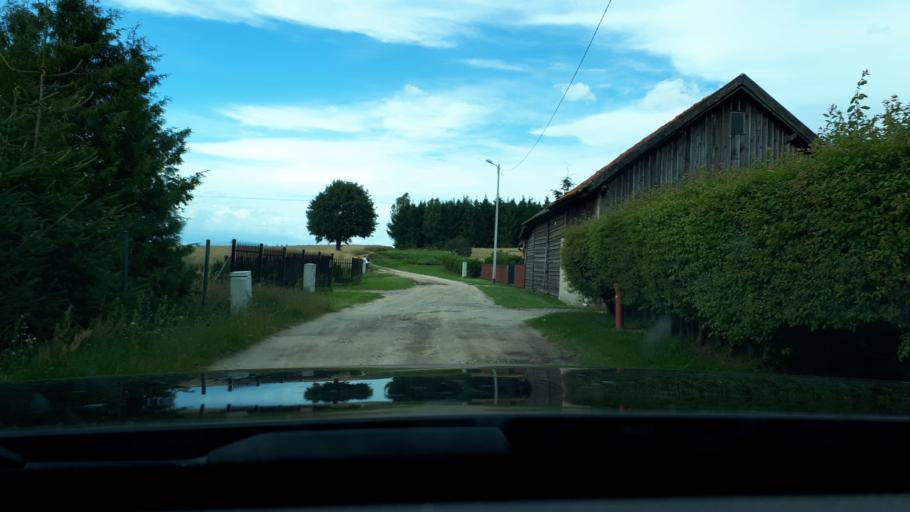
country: PL
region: Warmian-Masurian Voivodeship
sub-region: Powiat ostrodzki
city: Ostroda
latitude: 53.6796
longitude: 20.0440
